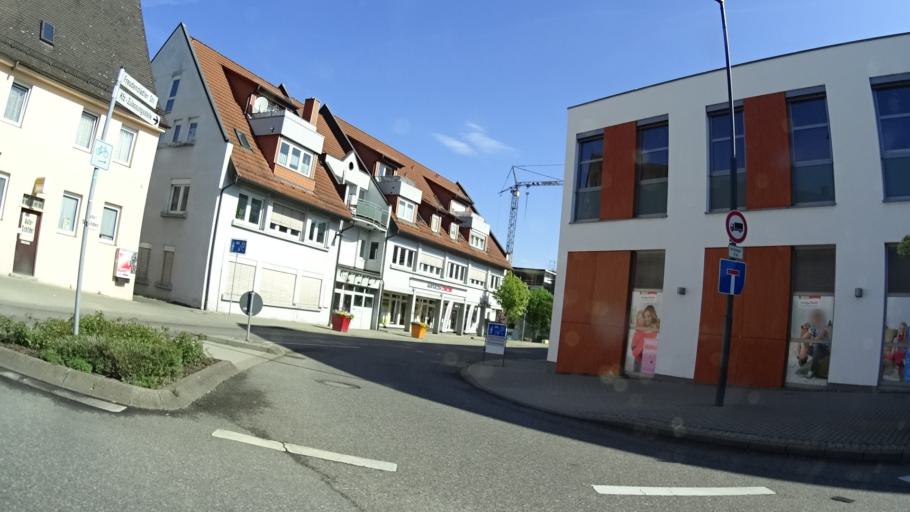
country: DE
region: Baden-Wuerttemberg
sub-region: Karlsruhe Region
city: Nagold
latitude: 48.5492
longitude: 8.7219
